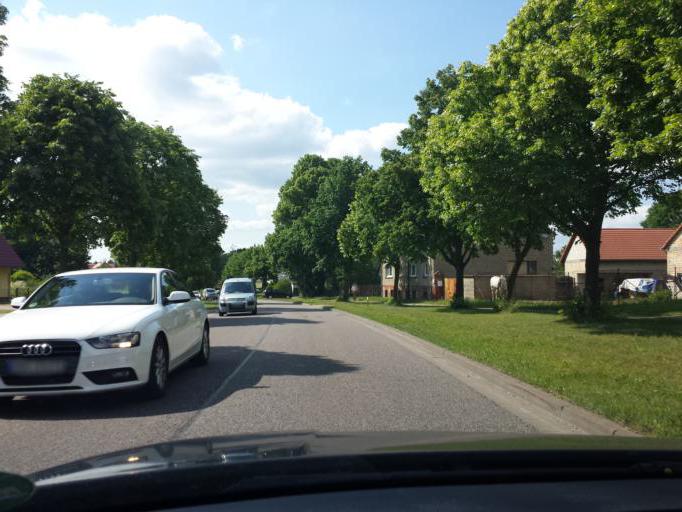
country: DE
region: Brandenburg
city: Ruthnick
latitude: 52.9057
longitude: 12.9668
